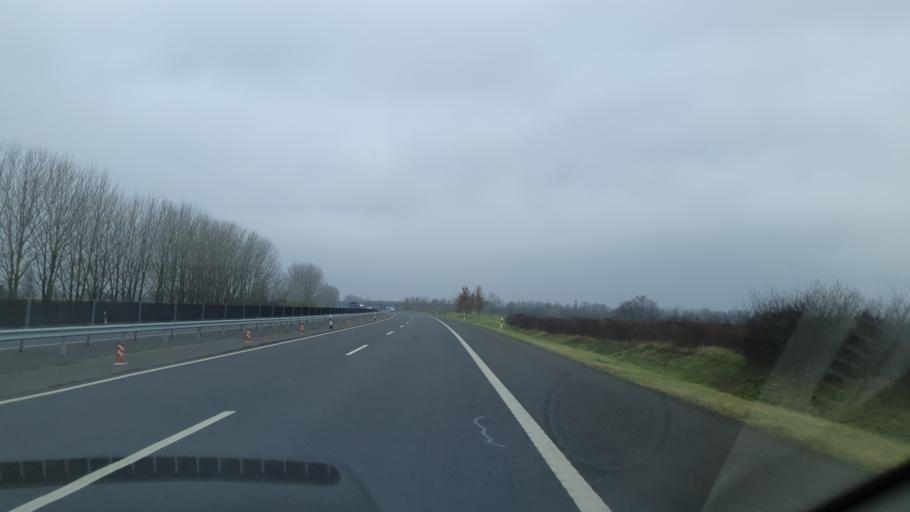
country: HU
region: Szabolcs-Szatmar-Bereg
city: Nyiregyhaza
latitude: 47.8998
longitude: 21.6741
